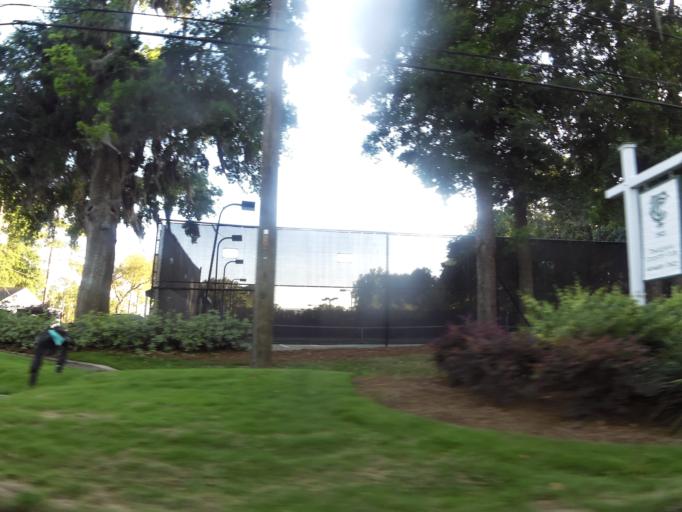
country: US
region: Florida
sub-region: Clay County
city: Orange Park
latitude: 30.2473
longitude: -81.6869
